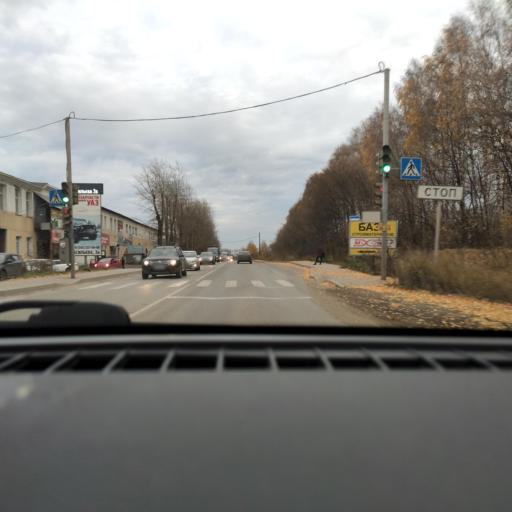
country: RU
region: Perm
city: Perm
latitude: 57.9567
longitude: 56.2157
